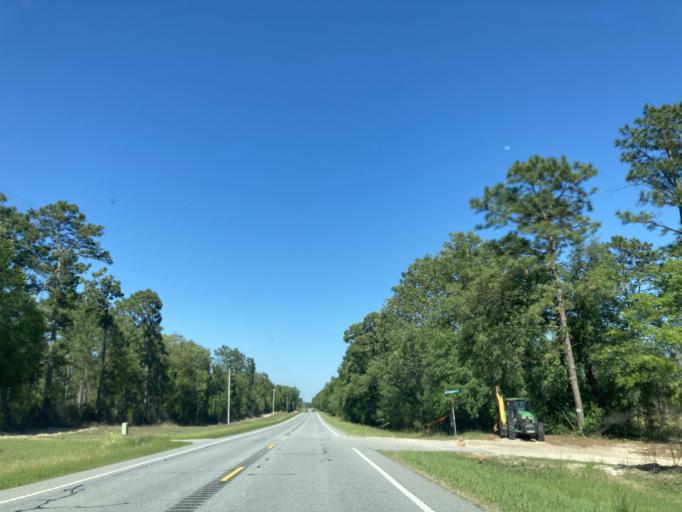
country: US
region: Georgia
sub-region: Baker County
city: Newton
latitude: 31.2843
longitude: -84.3666
